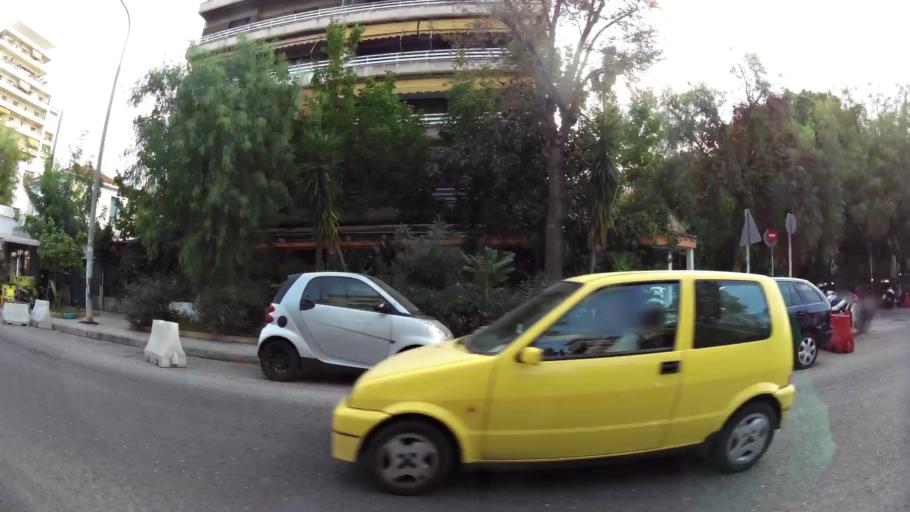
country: GR
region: Attica
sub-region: Nomarchia Athinas
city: Galatsi
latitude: 38.0168
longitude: 23.7396
